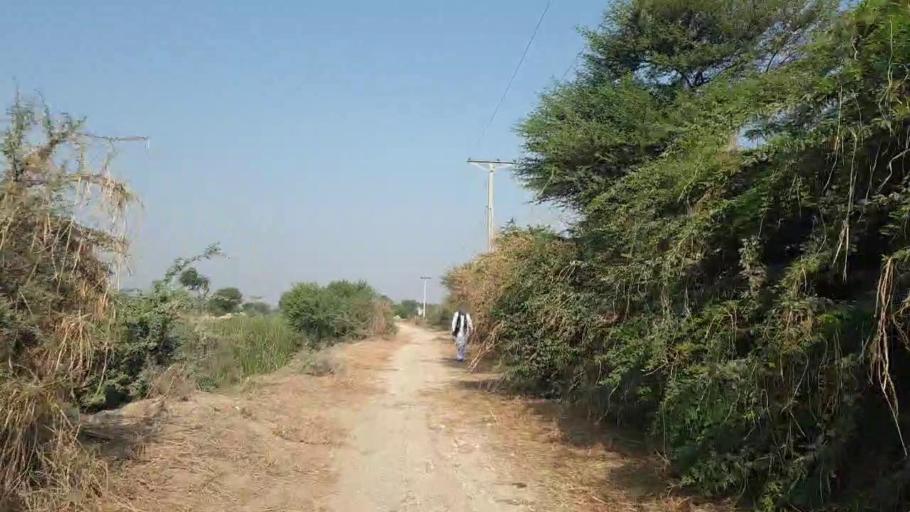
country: PK
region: Sindh
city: Matli
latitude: 24.9868
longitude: 68.6266
